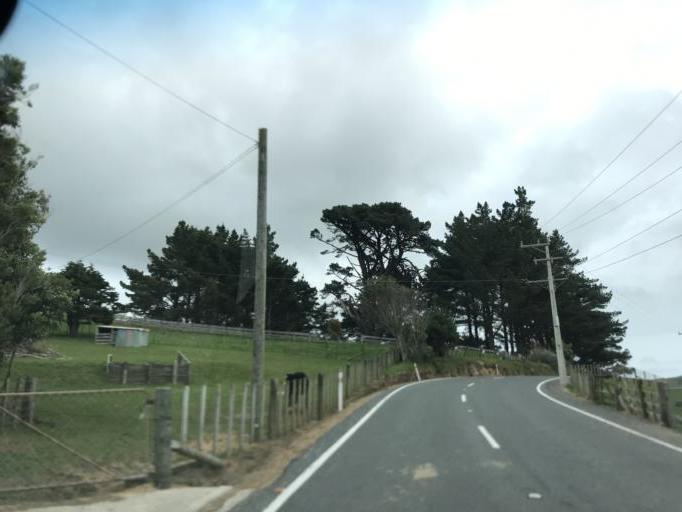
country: NZ
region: Wellington
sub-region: Porirua City
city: Porirua
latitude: -41.1800
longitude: 174.7971
